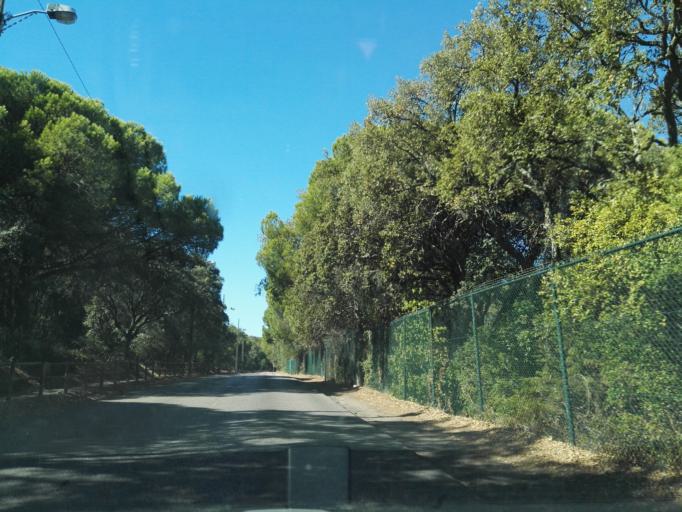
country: PT
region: Lisbon
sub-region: Odivelas
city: Pontinha
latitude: 38.7373
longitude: -9.1841
